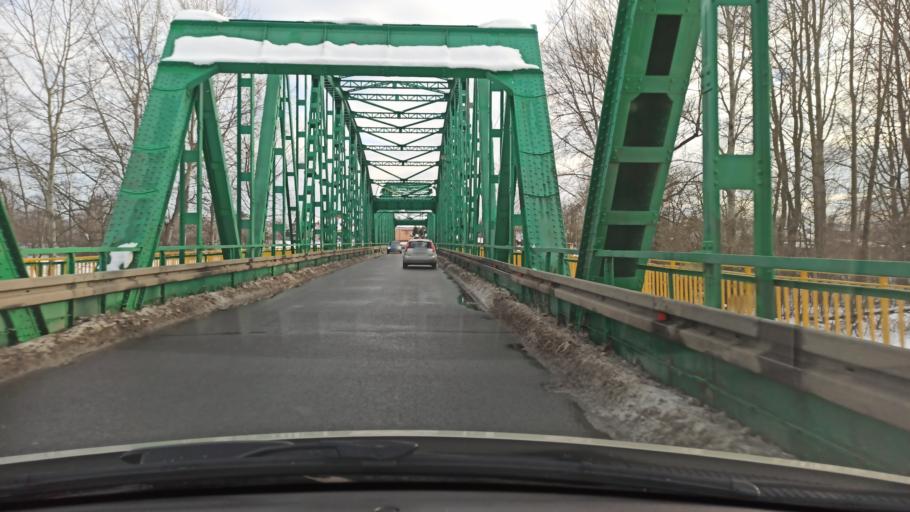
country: PL
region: Subcarpathian Voivodeship
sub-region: Powiat przeworski
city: Tryncza
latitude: 50.1632
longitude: 22.5468
